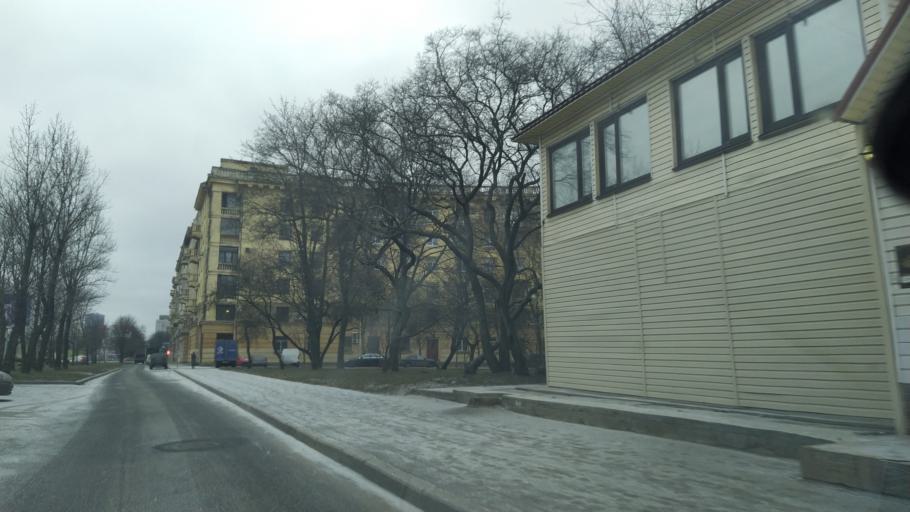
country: RU
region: St.-Petersburg
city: Kupchino
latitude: 59.8357
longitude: 30.3361
